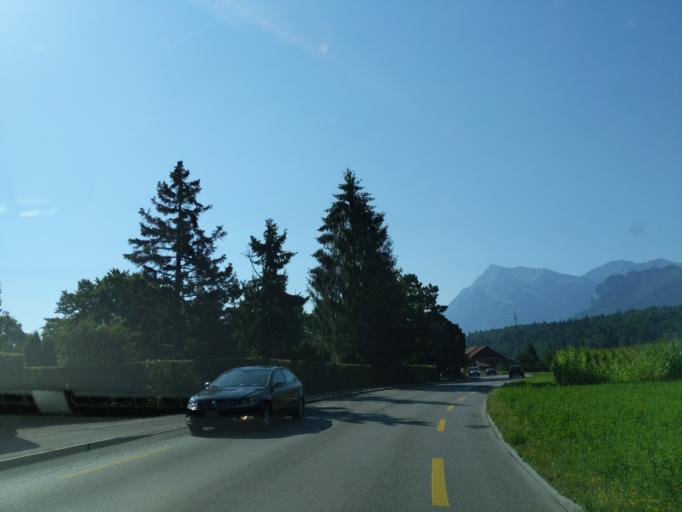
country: CH
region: Bern
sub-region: Thun District
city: Thun
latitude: 46.7318
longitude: 7.6128
